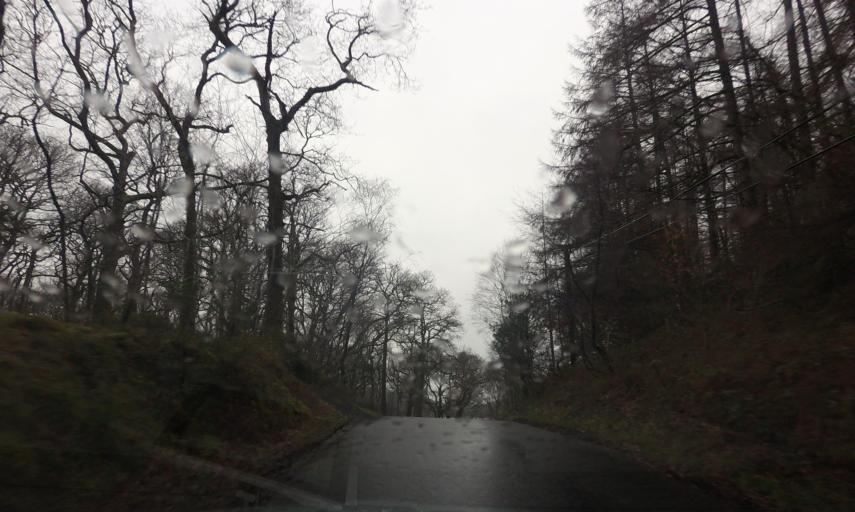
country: GB
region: Scotland
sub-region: West Dunbartonshire
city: Balloch
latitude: 56.1298
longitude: -4.6092
